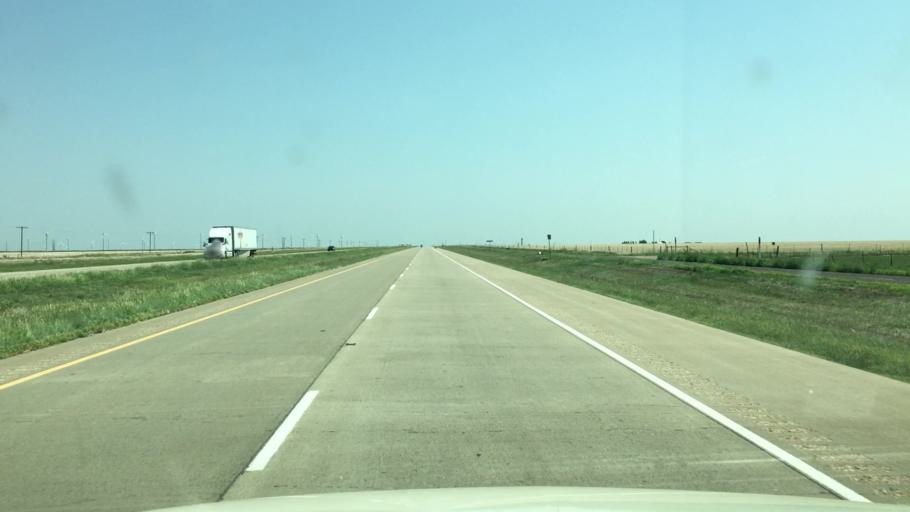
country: US
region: Texas
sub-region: Oldham County
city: Vega
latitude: 35.2727
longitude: -102.6123
